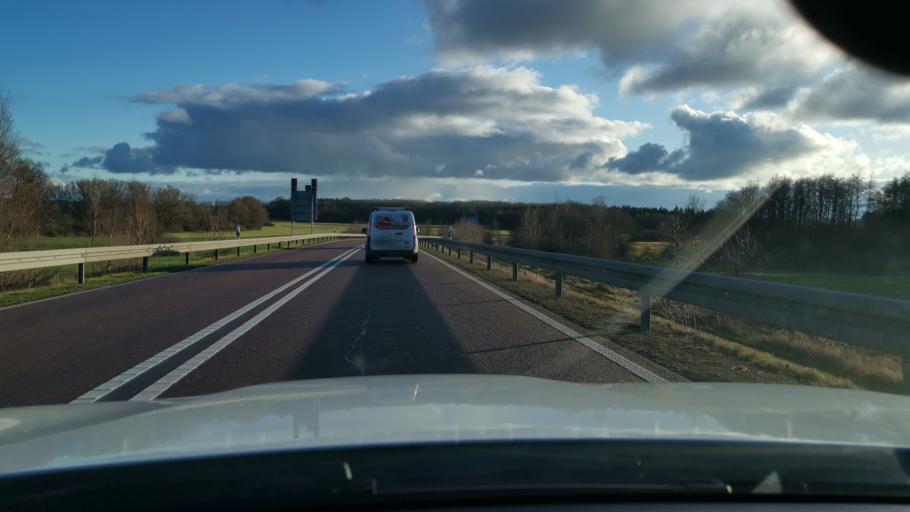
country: DE
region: Mecklenburg-Vorpommern
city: Tessin
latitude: 54.0387
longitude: 12.4102
